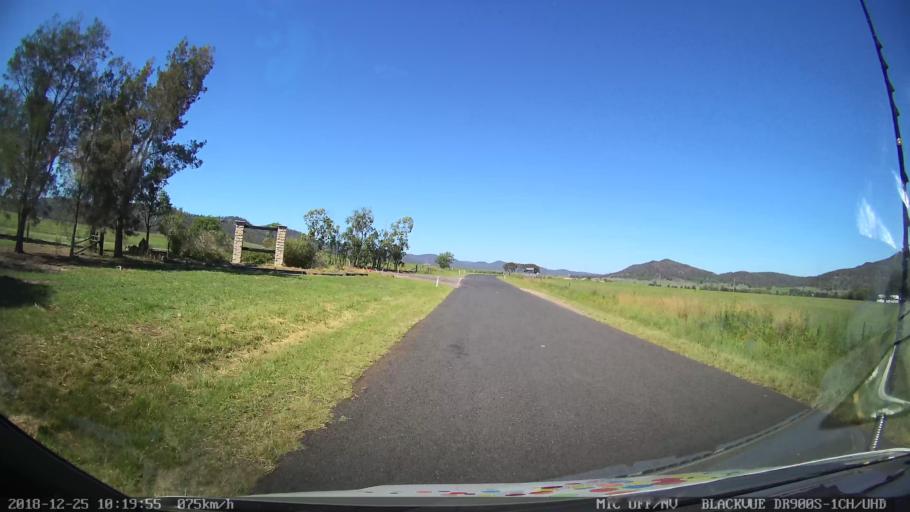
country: AU
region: New South Wales
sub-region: Muswellbrook
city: Denman
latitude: -32.3550
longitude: 150.5545
